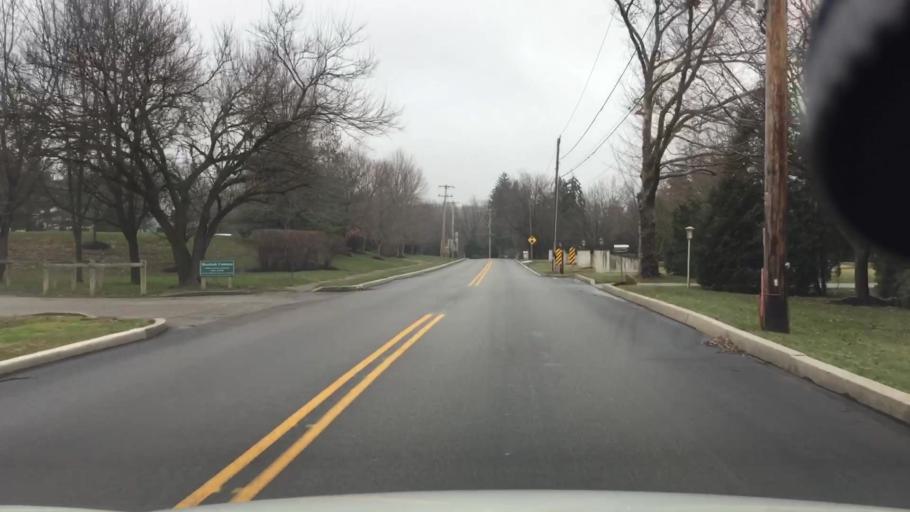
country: US
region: Pennsylvania
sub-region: Montgomery County
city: Dresher
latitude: 40.1546
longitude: -75.1790
